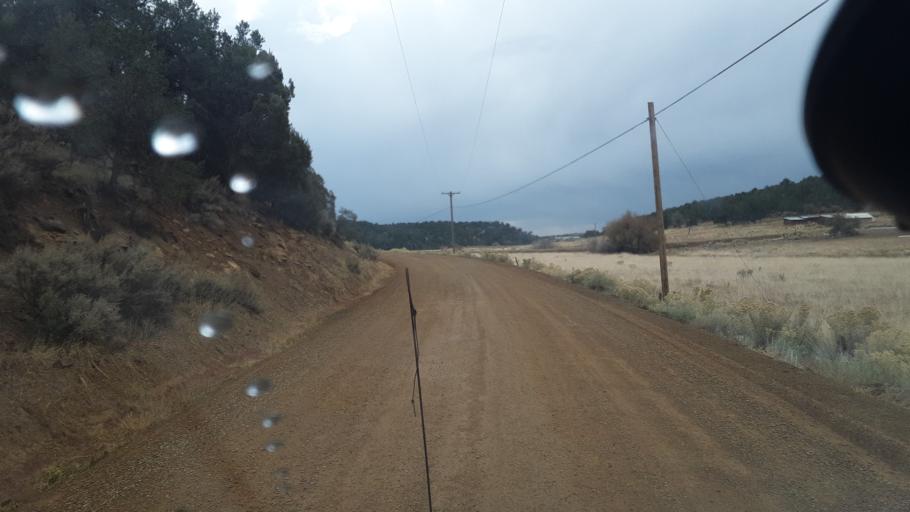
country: US
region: Colorado
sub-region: Montezuma County
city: Mancos
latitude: 37.2033
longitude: -108.1390
